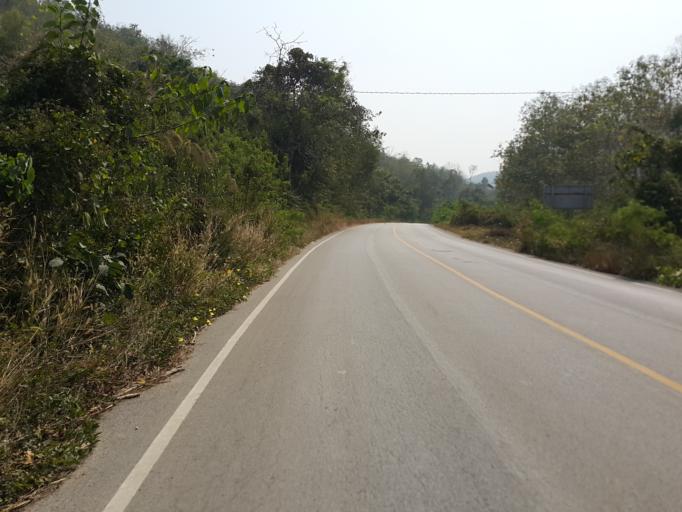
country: TH
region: Sukhothai
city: Thung Saliam
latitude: 17.3395
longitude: 99.4741
